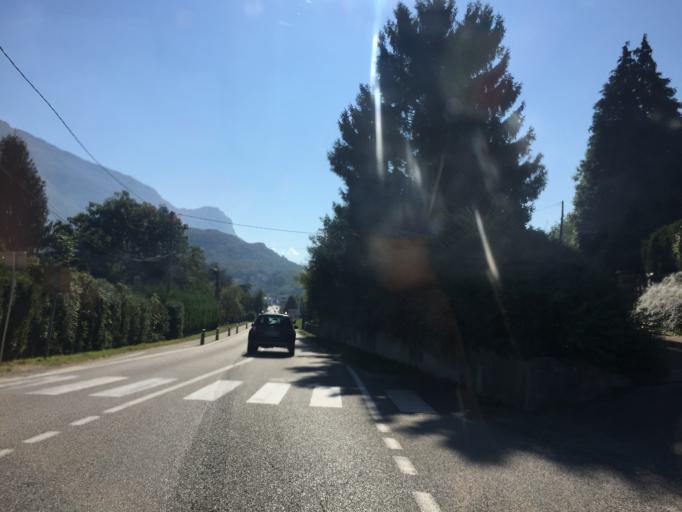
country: FR
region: Rhone-Alpes
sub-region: Departement de la Savoie
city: Challes-les-Eaux
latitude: 45.5437
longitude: 5.9839
